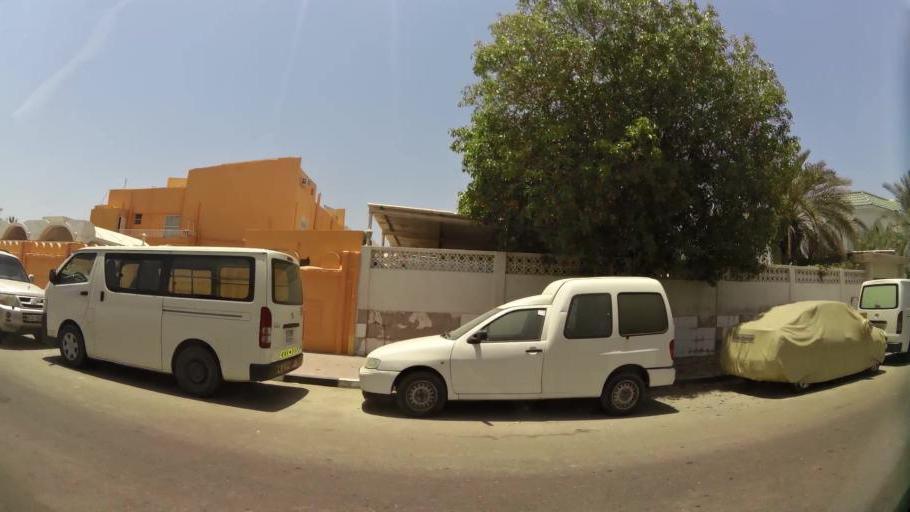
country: AE
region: Ash Shariqah
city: Sharjah
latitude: 25.2913
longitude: 55.3369
